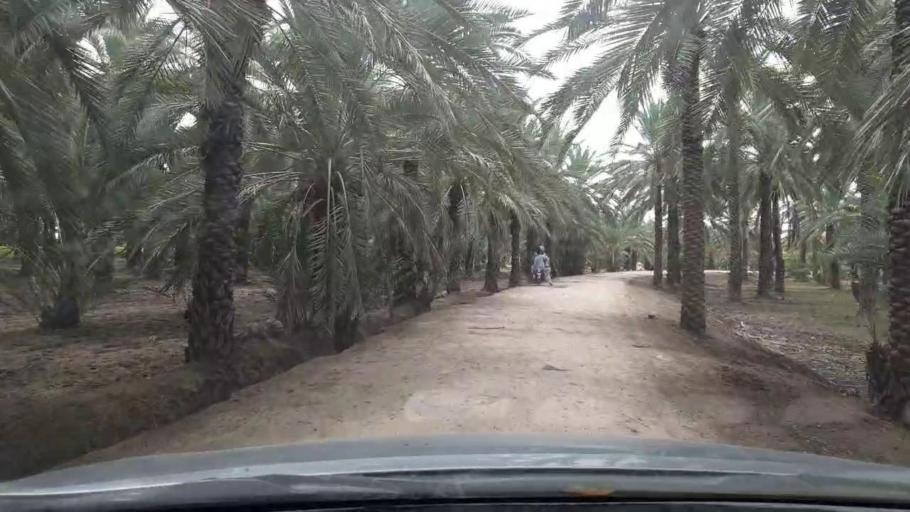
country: PK
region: Sindh
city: Khairpur
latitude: 27.4595
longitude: 68.7193
